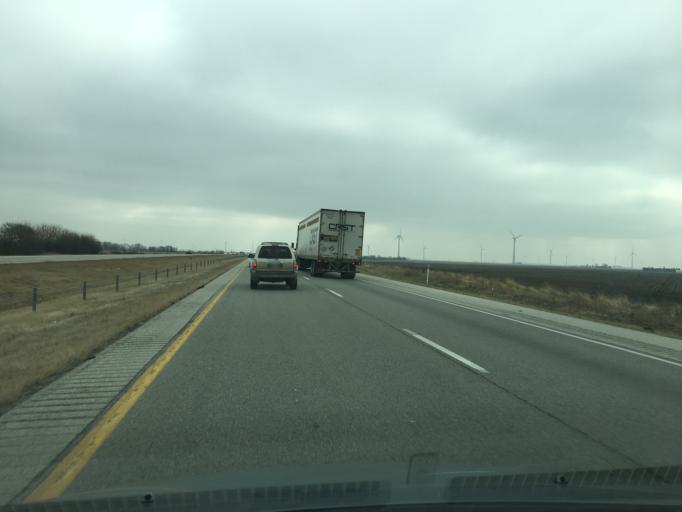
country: US
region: Indiana
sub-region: White County
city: Wolcott
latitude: 40.6294
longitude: -87.0008
